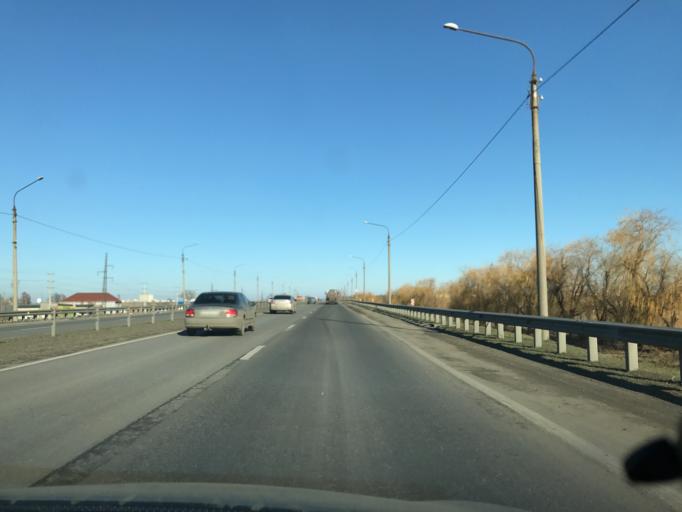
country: RU
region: Rostov
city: Bataysk
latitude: 47.1162
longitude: 39.7689
